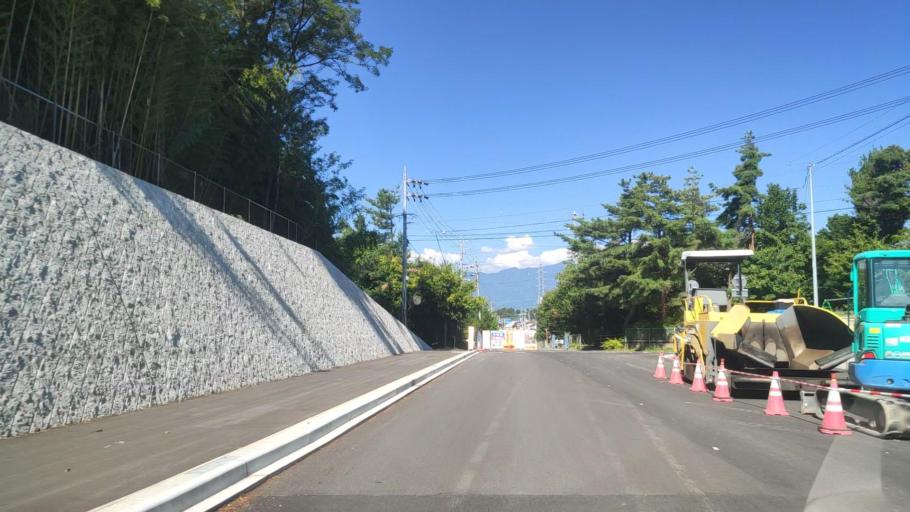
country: JP
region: Nagano
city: Shiojiri
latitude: 36.1503
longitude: 137.9409
